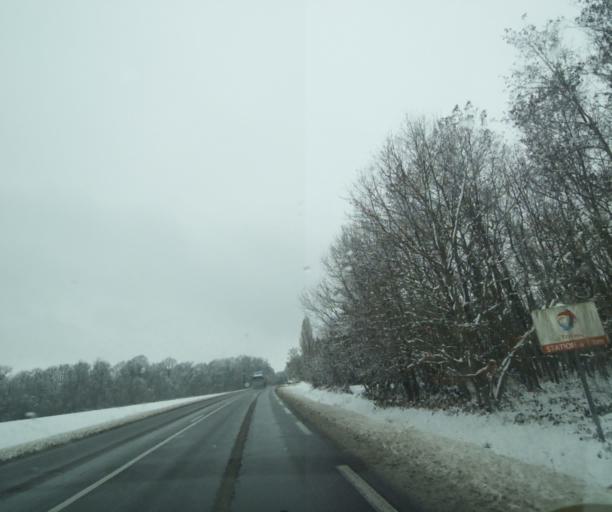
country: FR
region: Champagne-Ardenne
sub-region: Departement de la Haute-Marne
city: Montier-en-Der
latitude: 48.4941
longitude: 4.7810
